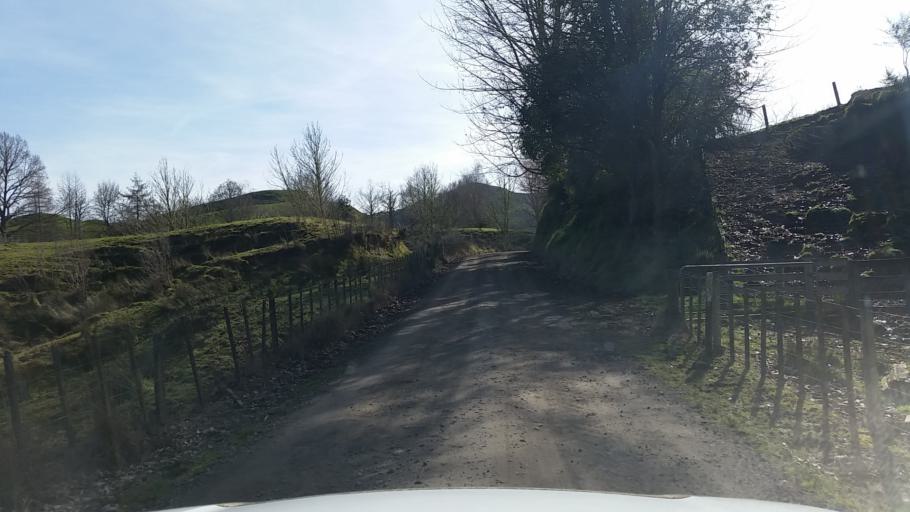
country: NZ
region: Taranaki
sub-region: South Taranaki District
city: Eltham
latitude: -39.3526
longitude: 174.5132
